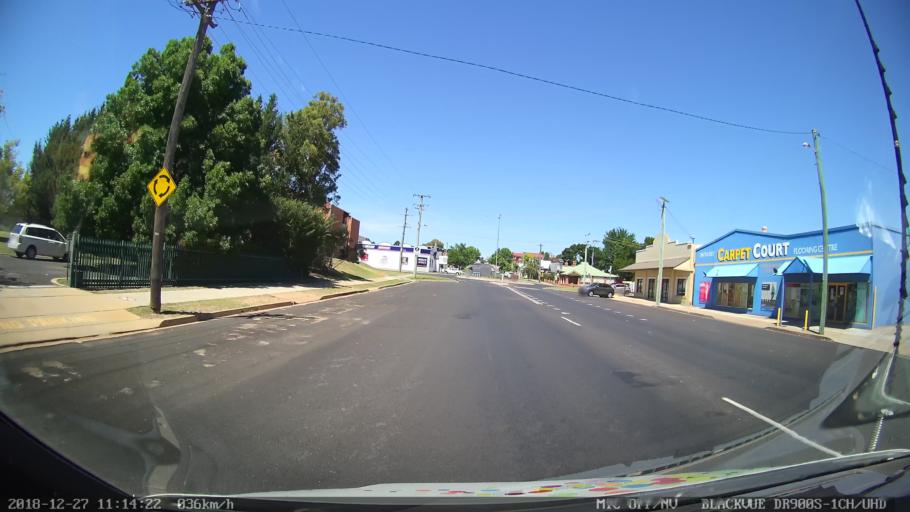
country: AU
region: New South Wales
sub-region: Bathurst Regional
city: Bathurst
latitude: -33.4193
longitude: 149.5750
